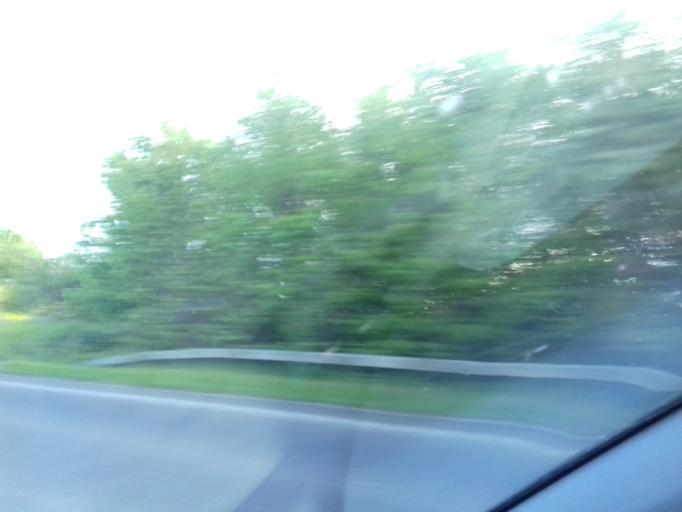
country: IE
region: Leinster
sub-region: South Dublin
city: Rathcoole
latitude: 53.2854
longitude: -6.4631
